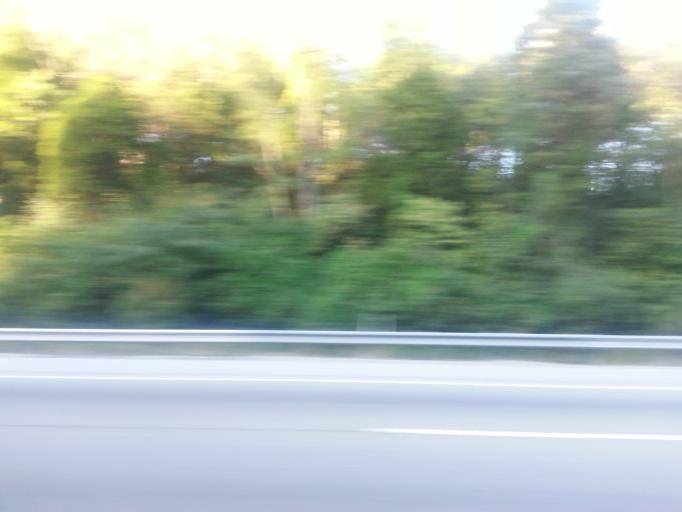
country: US
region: Tennessee
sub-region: Knox County
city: Knoxville
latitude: 36.0146
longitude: -83.9803
